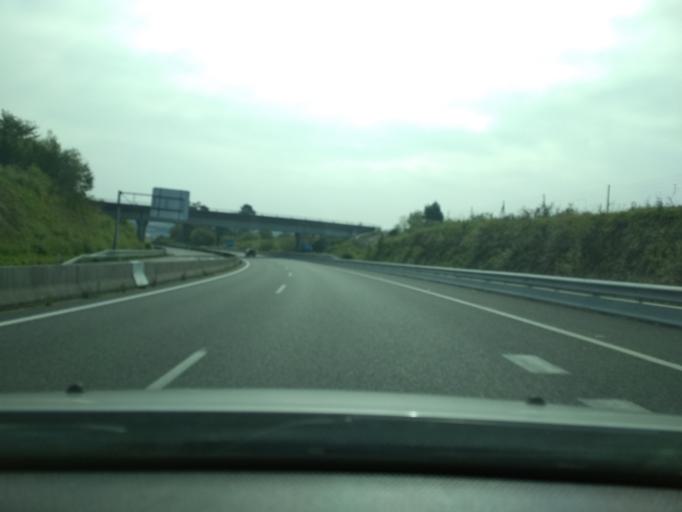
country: ES
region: Galicia
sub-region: Provincia da Coruna
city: Rianxo
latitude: 42.6691
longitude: -8.8251
